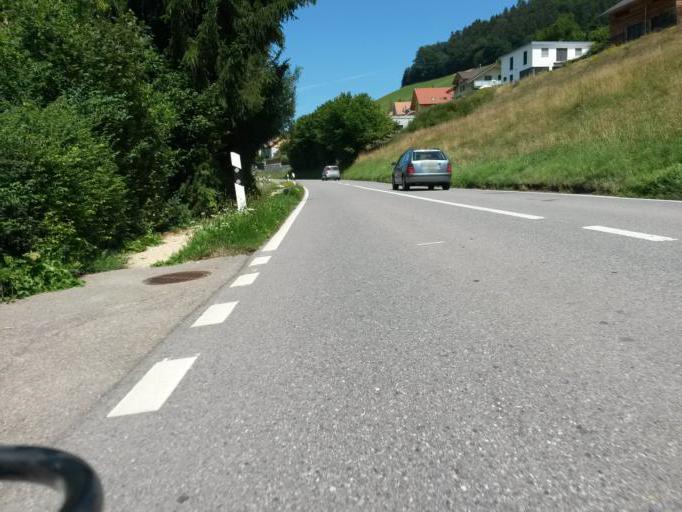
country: CH
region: Bern
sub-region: Bern-Mittelland District
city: Walkringen
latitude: 46.9396
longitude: 7.6167
